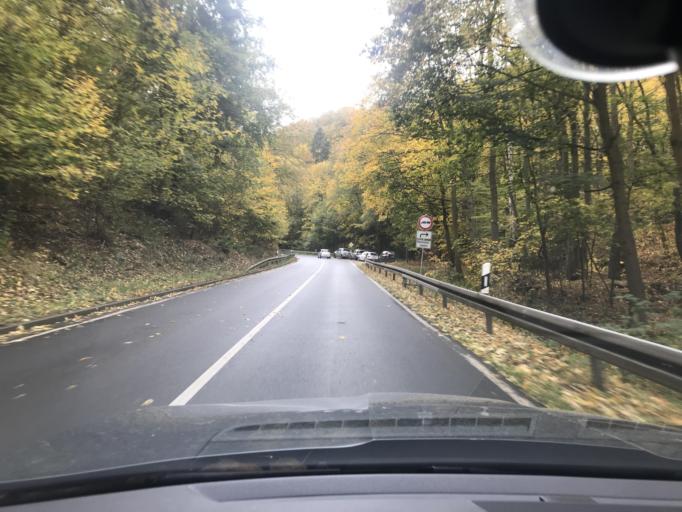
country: DE
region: Saxony-Anhalt
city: Thale
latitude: 51.7320
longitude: 11.0312
